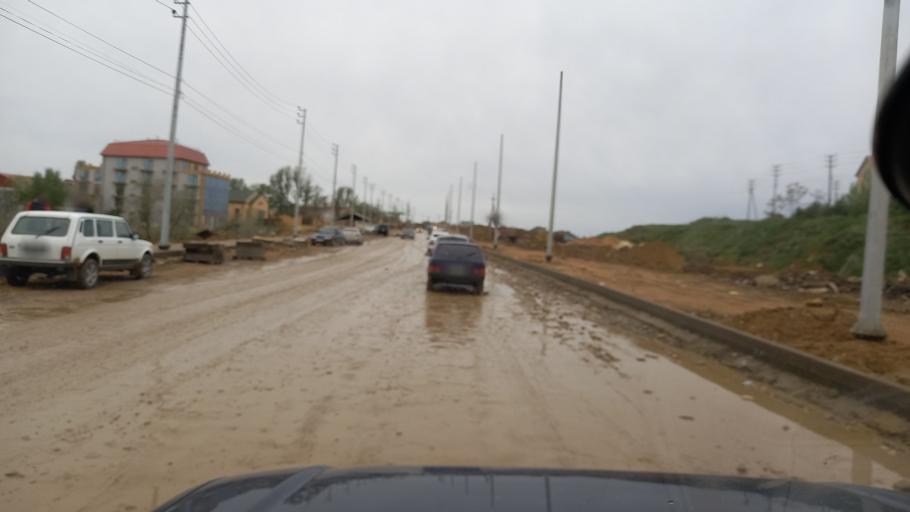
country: RU
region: Dagestan
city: Derbent
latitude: 42.0965
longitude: 48.2873
